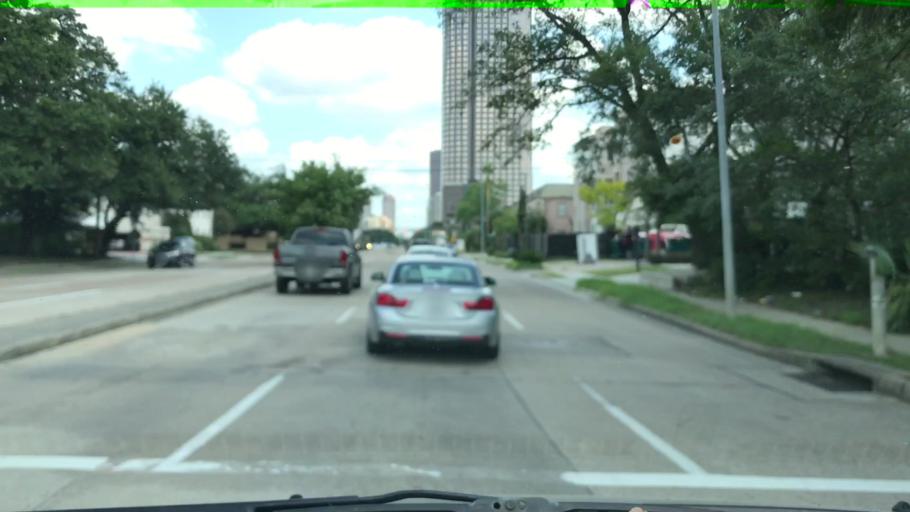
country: US
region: Texas
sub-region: Harris County
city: Hunters Creek Village
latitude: 29.7498
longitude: -95.4886
